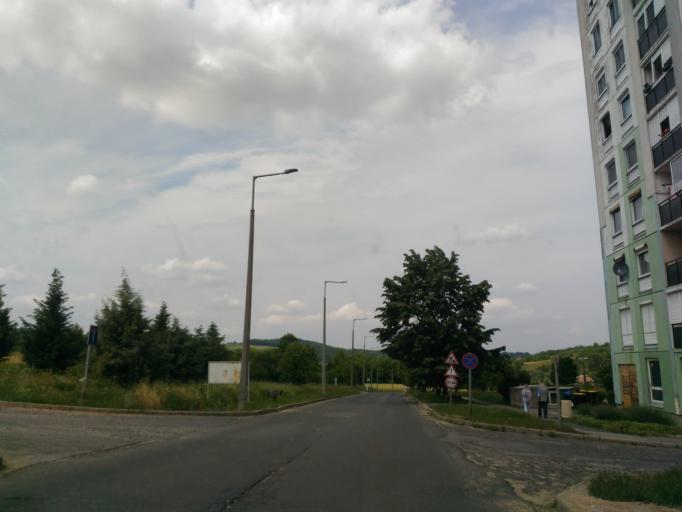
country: HU
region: Baranya
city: Komlo
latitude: 46.1901
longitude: 18.2307
